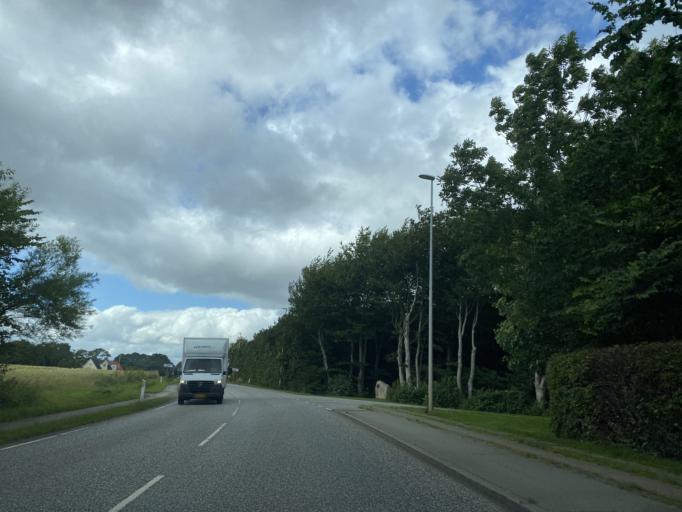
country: DK
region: Central Jutland
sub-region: Silkeborg Kommune
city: Svejbaek
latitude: 56.2286
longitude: 9.6296
